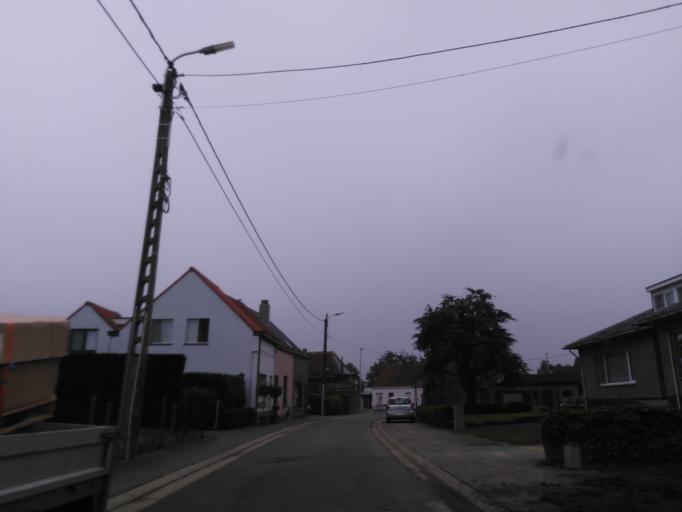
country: BE
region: Flanders
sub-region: Provincie Oost-Vlaanderen
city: Sint-Gillis-Waas
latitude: 51.2240
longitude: 4.1887
